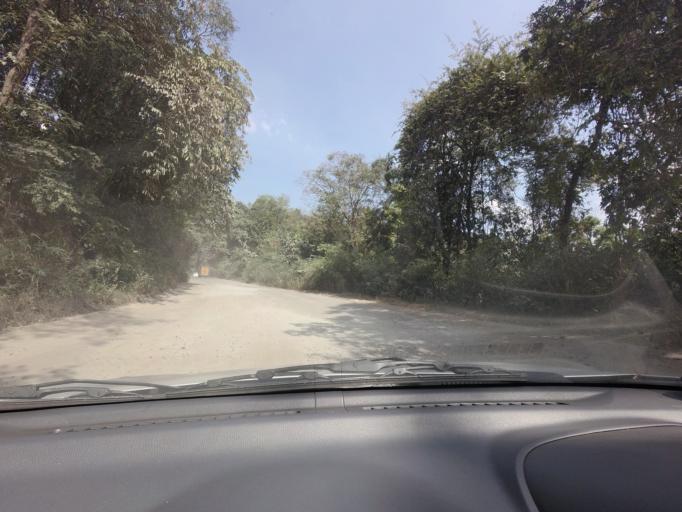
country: IN
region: Karnataka
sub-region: Hassan
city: Sakleshpur
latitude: 12.8295
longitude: 75.5916
